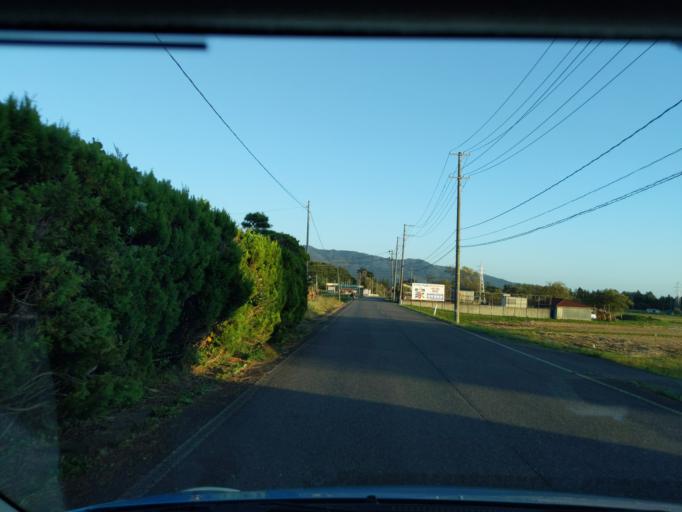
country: JP
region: Iwate
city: Mizusawa
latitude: 39.0545
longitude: 141.1155
